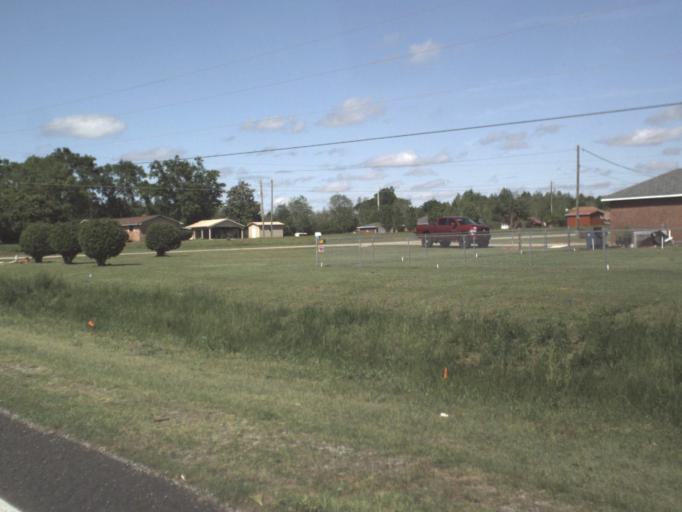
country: US
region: Florida
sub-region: Escambia County
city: Molino
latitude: 30.7075
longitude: -87.3501
